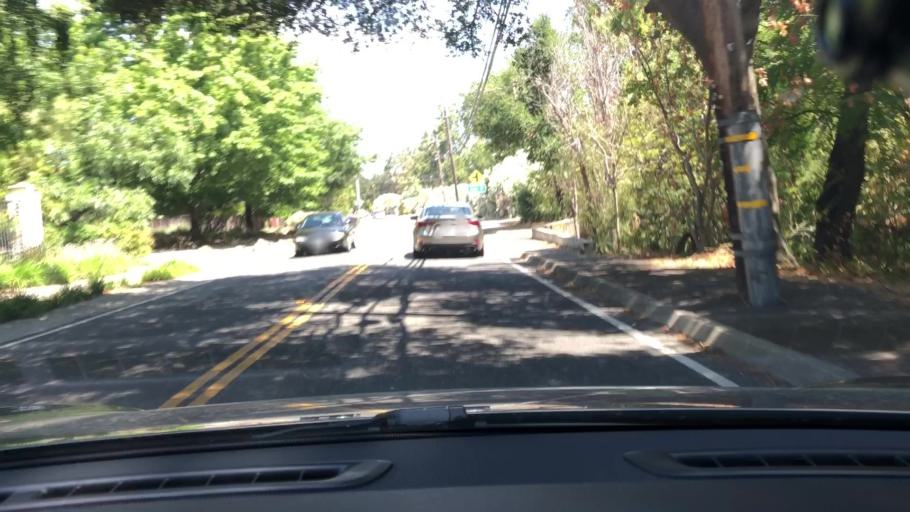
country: US
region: California
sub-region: Santa Clara County
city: Monte Sereno
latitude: 37.2606
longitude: -121.9921
